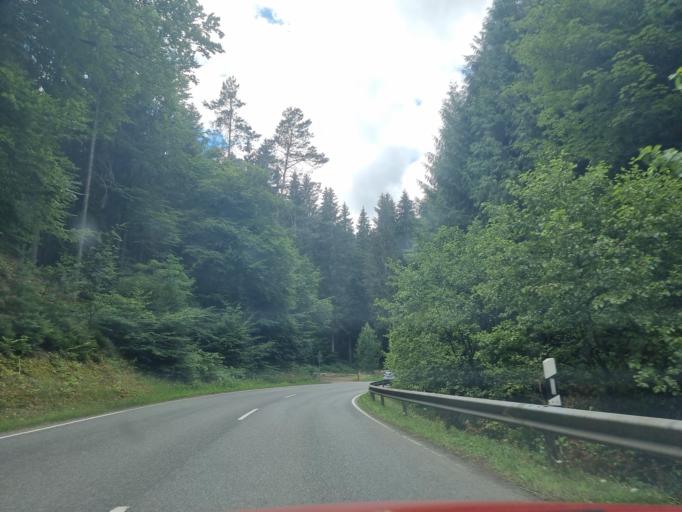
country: DE
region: Rheinland-Pfalz
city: Kenn
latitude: 49.8451
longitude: 6.7040
